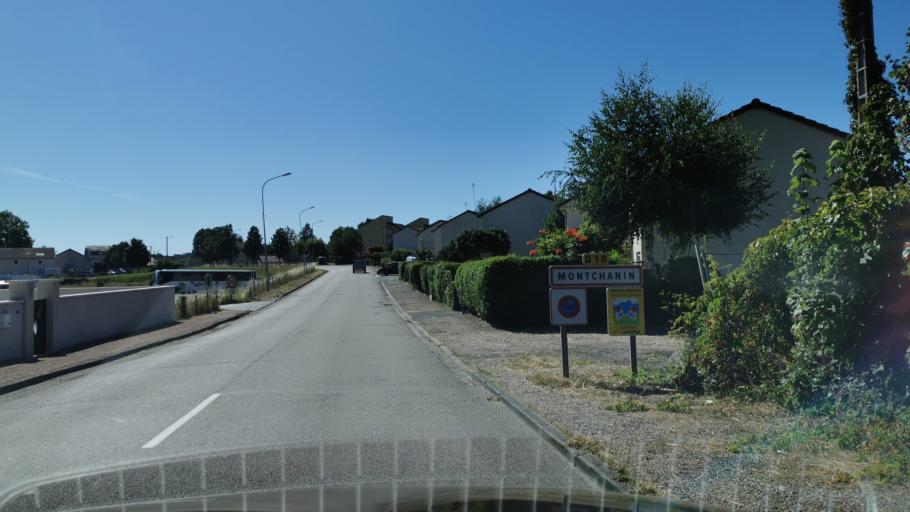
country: FR
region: Bourgogne
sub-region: Departement de Saone-et-Loire
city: Montchanin
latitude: 46.7601
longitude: 4.4768
